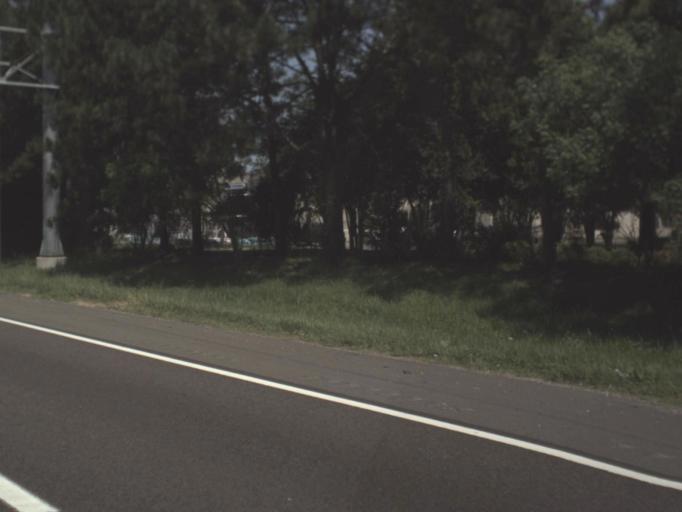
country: US
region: Florida
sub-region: Duval County
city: Jacksonville
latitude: 30.3156
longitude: -81.7564
